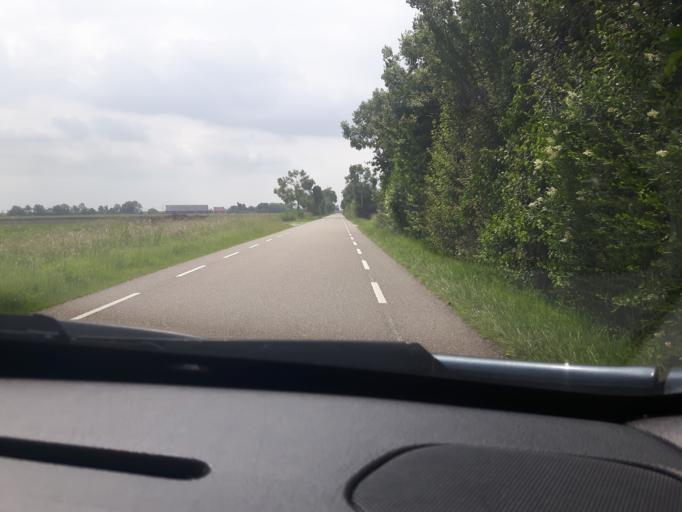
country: NL
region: Zeeland
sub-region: Gemeente Terneuzen
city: Terneuzen
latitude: 51.4053
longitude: 3.8401
